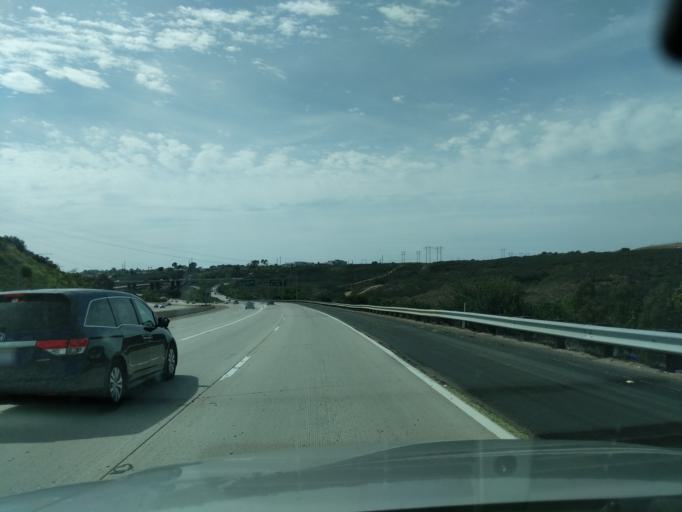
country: US
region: California
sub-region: San Diego County
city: La Jolla
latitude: 32.8464
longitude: -117.1683
